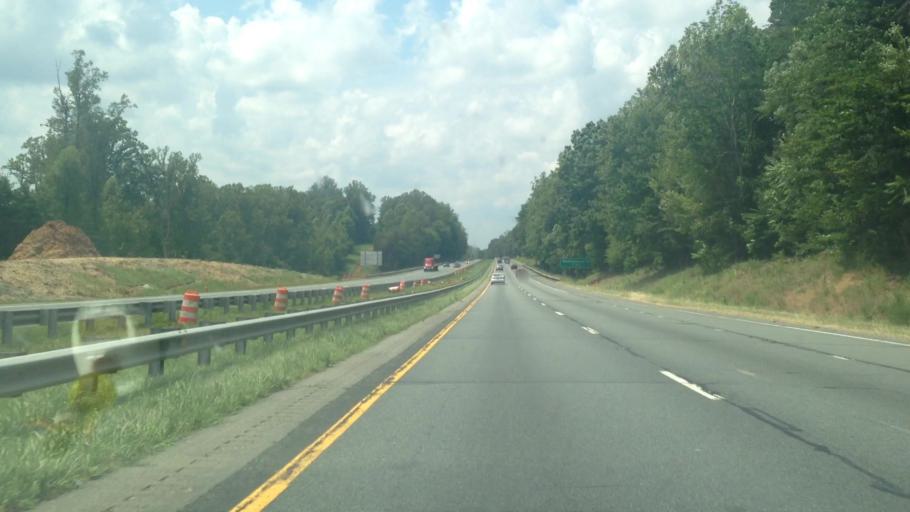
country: US
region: North Carolina
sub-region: Forsyth County
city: Rural Hall
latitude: 36.2137
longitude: -80.3060
